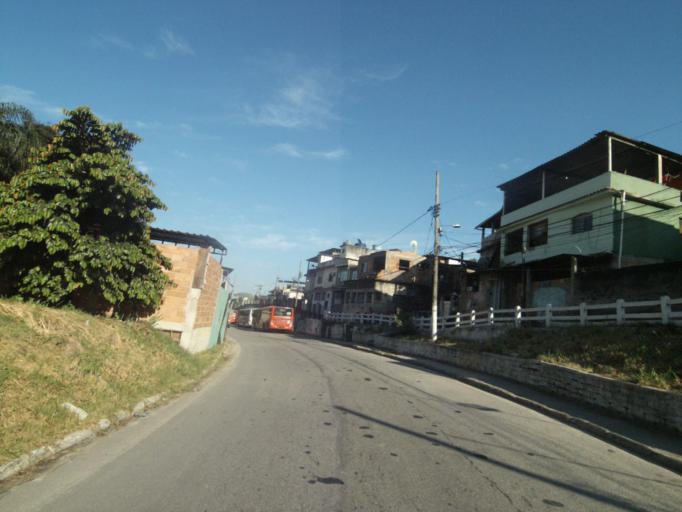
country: BR
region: Rio de Janeiro
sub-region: Niteroi
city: Niteroi
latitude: -22.8816
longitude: -43.0764
